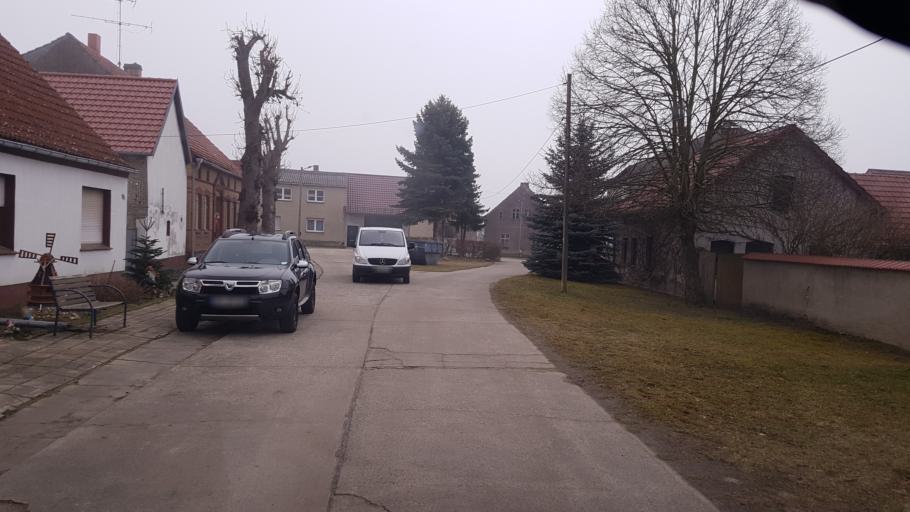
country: DE
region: Saxony-Anhalt
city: Holzdorf
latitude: 51.8612
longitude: 13.2141
